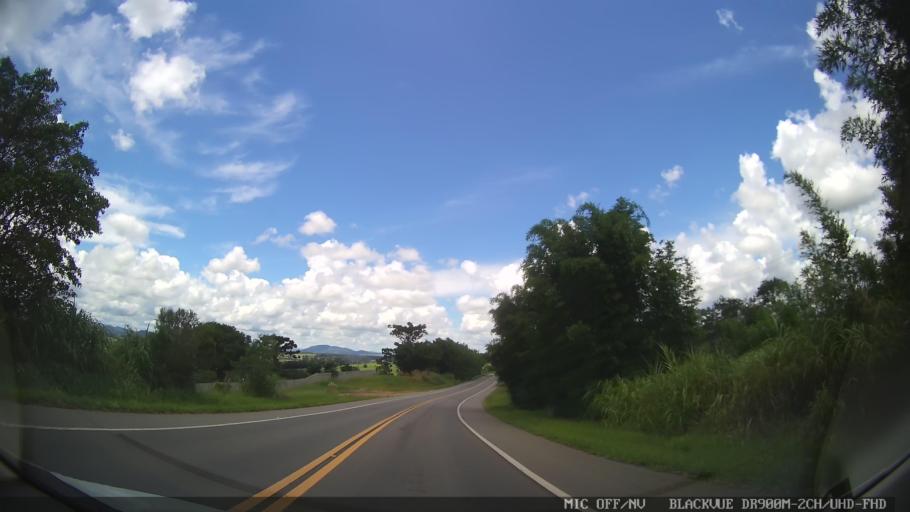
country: BR
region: Sao Paulo
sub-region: Braganca Paulista
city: Braganca Paulista
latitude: -22.8577
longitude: -46.6353
